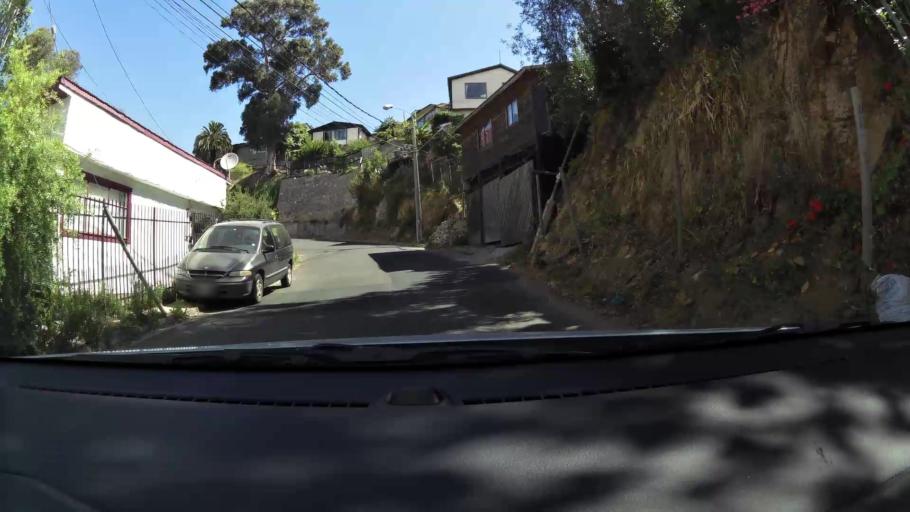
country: CL
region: Valparaiso
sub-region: Provincia de Valparaiso
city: Vina del Mar
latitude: -33.0396
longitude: -71.5773
